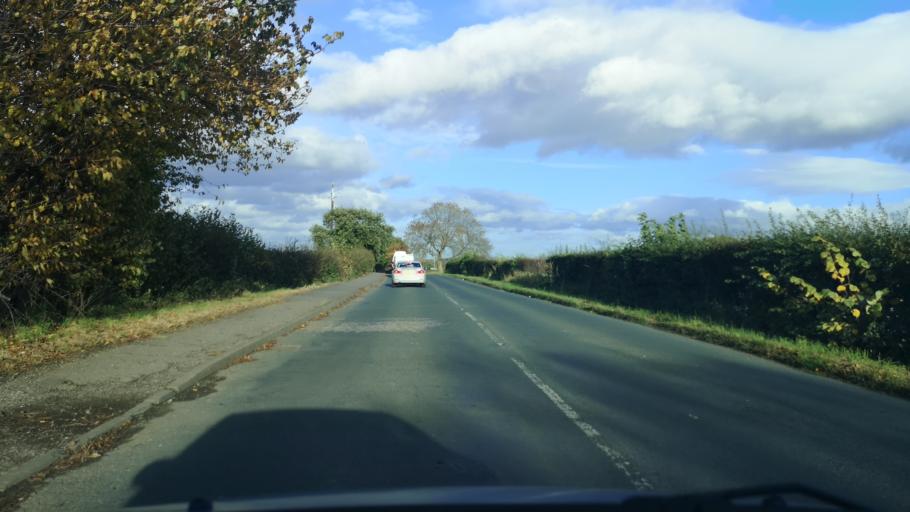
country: GB
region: England
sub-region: City and Borough of Wakefield
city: Crigglestone
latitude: 53.6210
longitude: -1.5593
